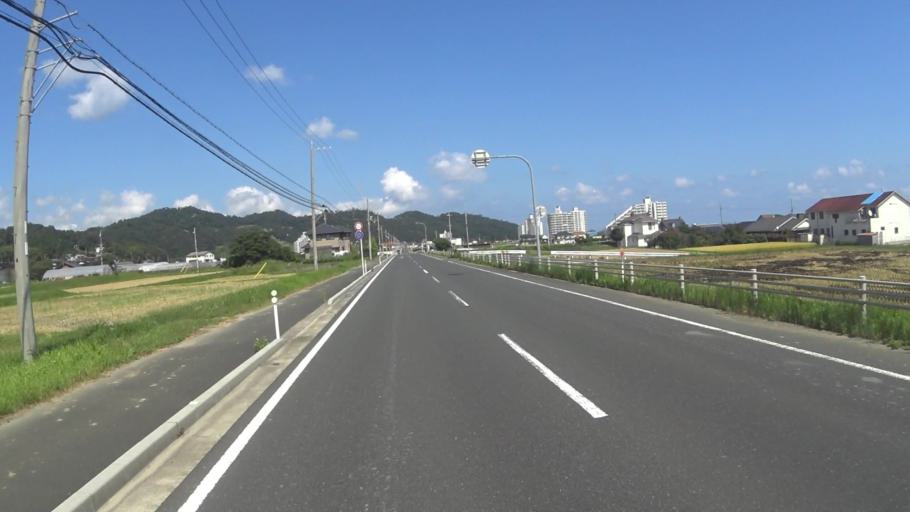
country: JP
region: Kyoto
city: Miyazu
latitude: 35.6065
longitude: 135.2237
